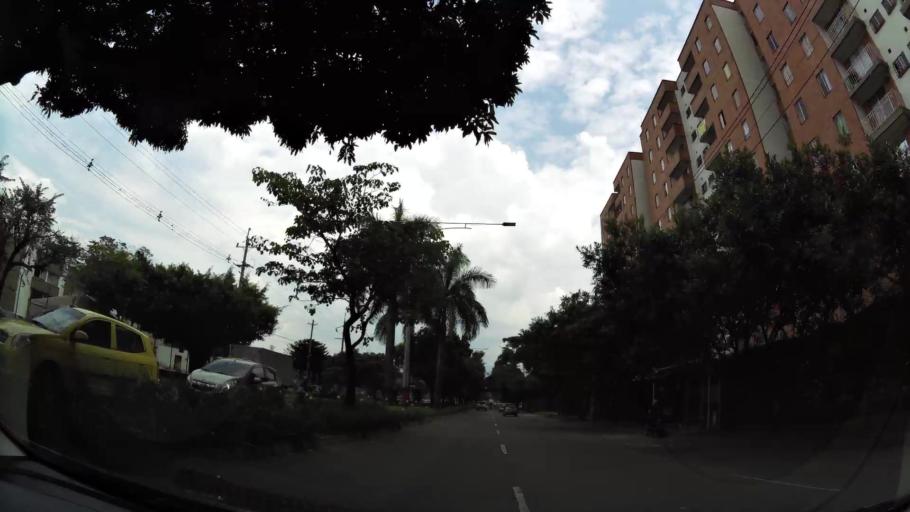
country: CO
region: Antioquia
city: Envigado
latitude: 6.1667
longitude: -75.5989
